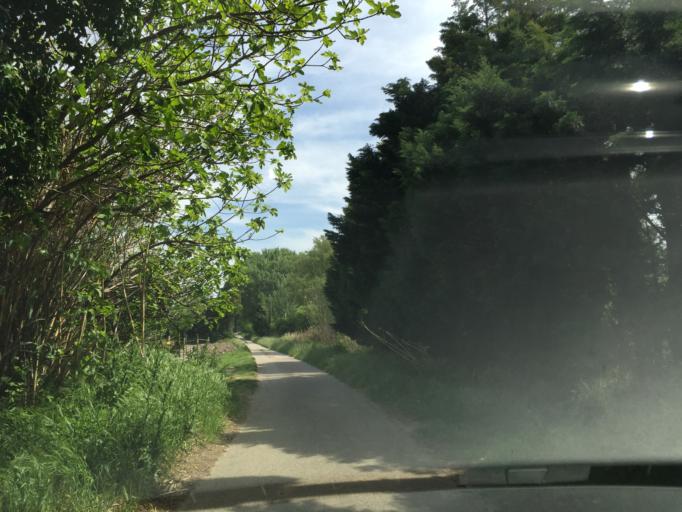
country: FR
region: Provence-Alpes-Cote d'Azur
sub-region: Departement du Vaucluse
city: Courthezon
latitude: 44.0891
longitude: 4.8584
